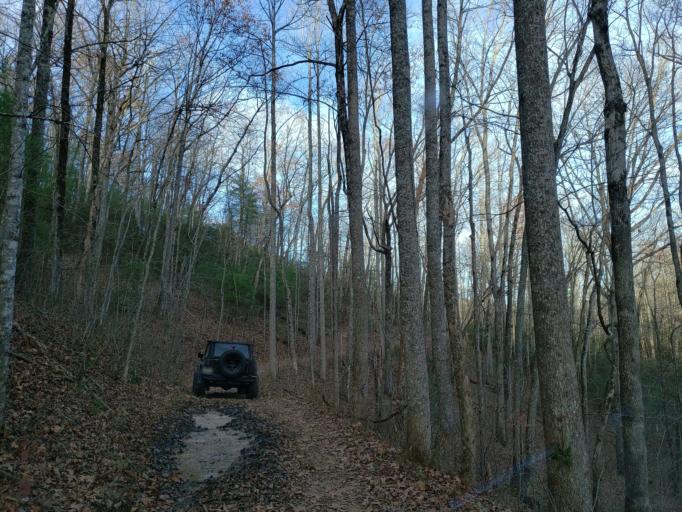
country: US
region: Georgia
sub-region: Lumpkin County
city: Dahlonega
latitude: 34.6600
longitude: -84.1085
